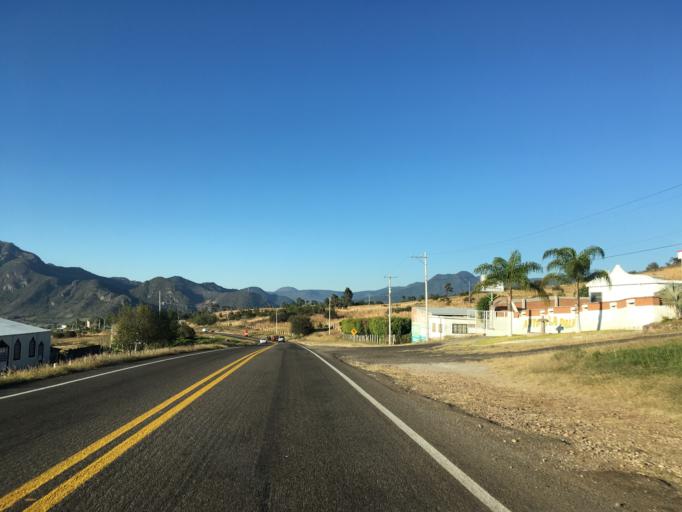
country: MX
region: Michoacan
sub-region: Tuxpan
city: La Soledad
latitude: 19.5227
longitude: -100.4725
